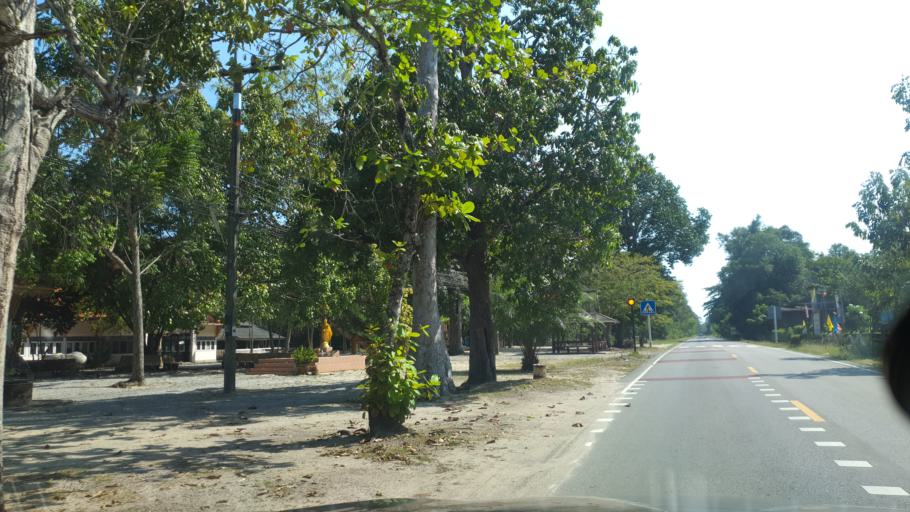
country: TH
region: Surat Thani
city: Tha Chana
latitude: 9.5858
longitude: 99.2021
